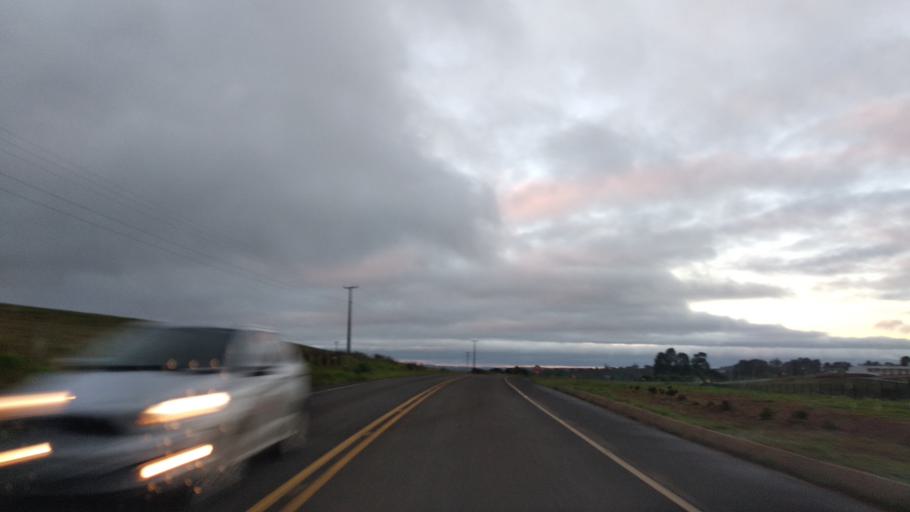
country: BR
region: Santa Catarina
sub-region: Campos Novos
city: Campos Novos
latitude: -27.3706
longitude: -51.2034
